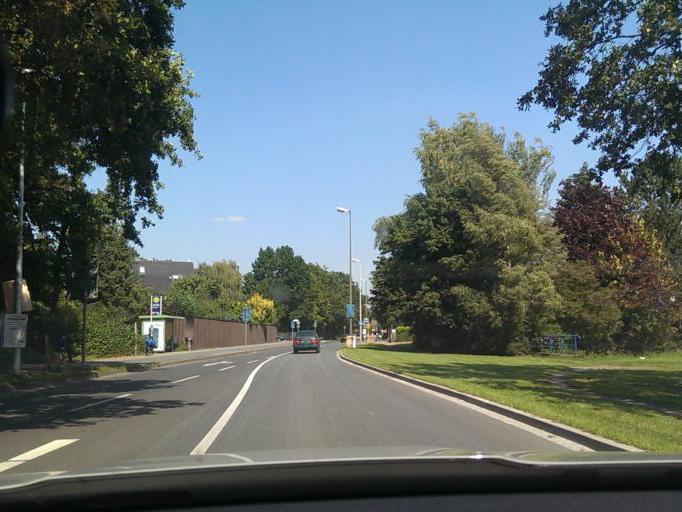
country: DE
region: Lower Saxony
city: Langenhagen
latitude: 52.4494
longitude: 9.7565
